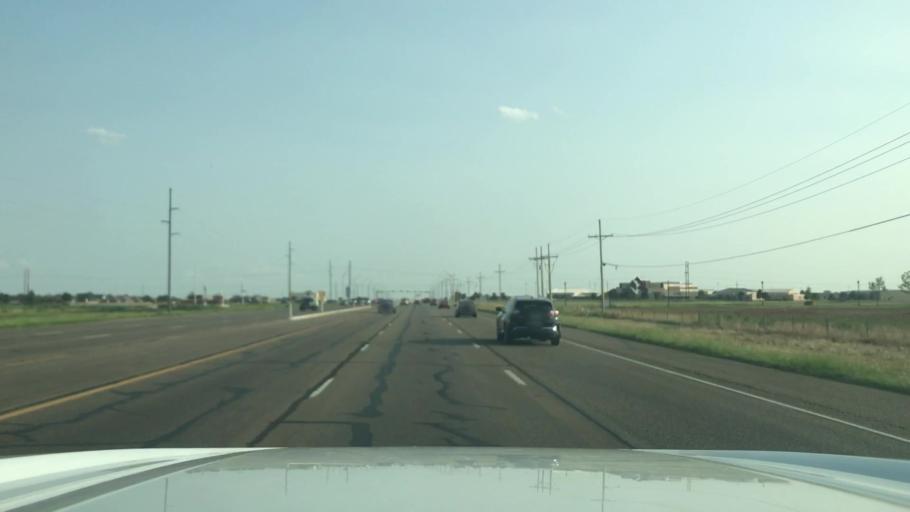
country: US
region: Texas
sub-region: Potter County
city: Amarillo
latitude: 35.1517
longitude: -101.9383
